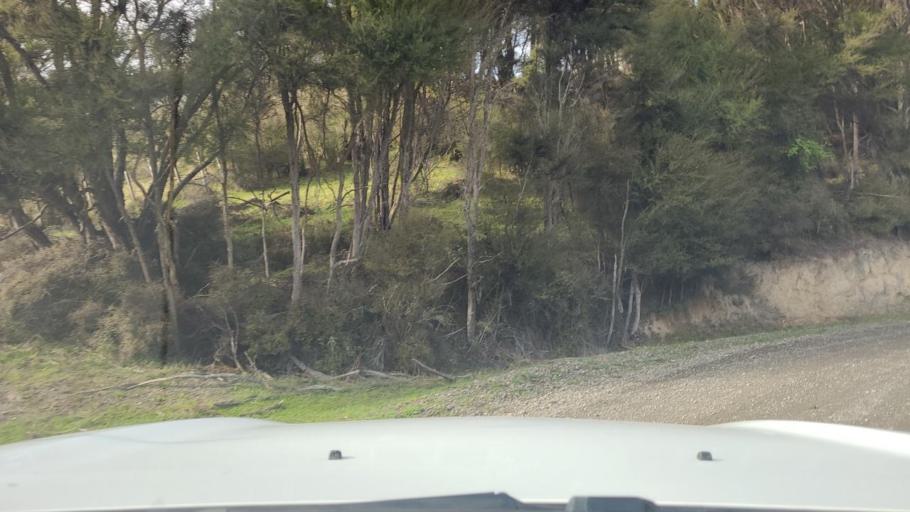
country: NZ
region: Wellington
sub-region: South Wairarapa District
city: Waipawa
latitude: -41.2567
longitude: 175.6920
